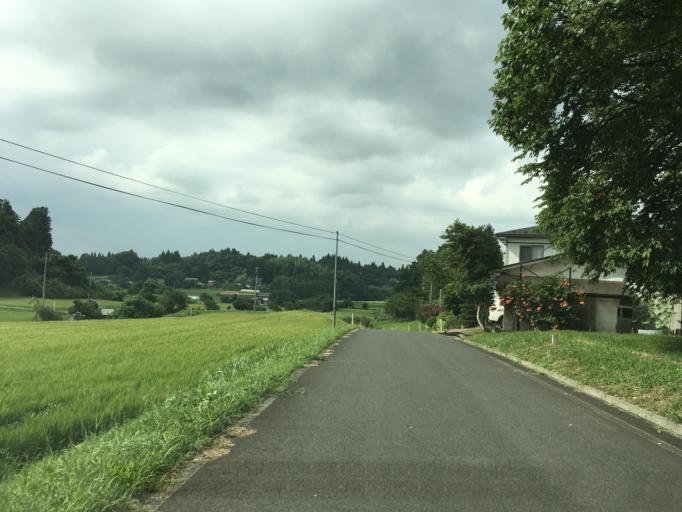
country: JP
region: Iwate
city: Ichinoseki
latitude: 38.8715
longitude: 141.3641
